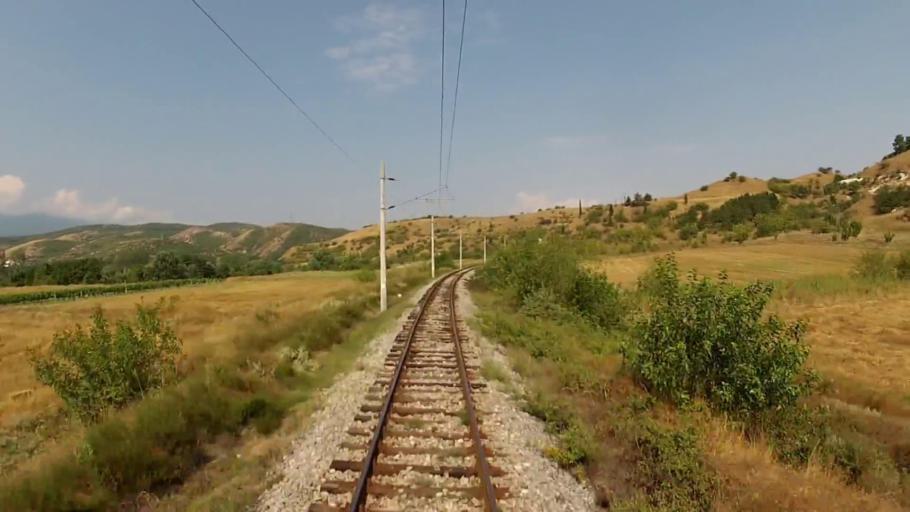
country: BG
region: Blagoevgrad
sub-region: Obshtina Petrich
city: Petrich
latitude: 41.4273
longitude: 23.3300
